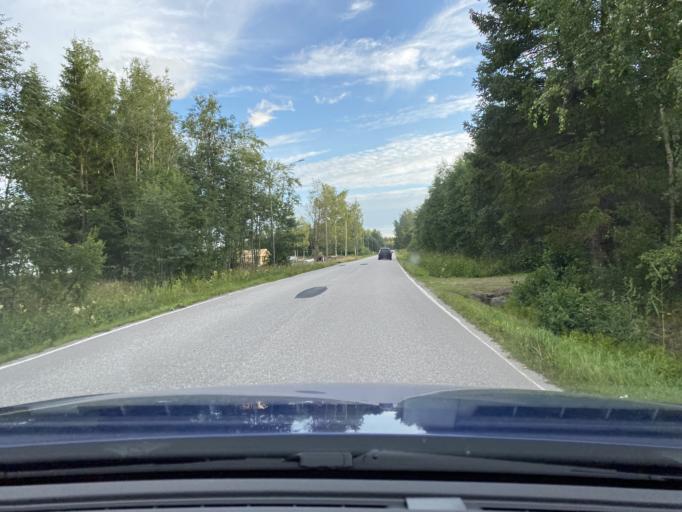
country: FI
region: Ostrobothnia
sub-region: Vaasa
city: Korsnaes
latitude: 62.9587
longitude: 21.1866
